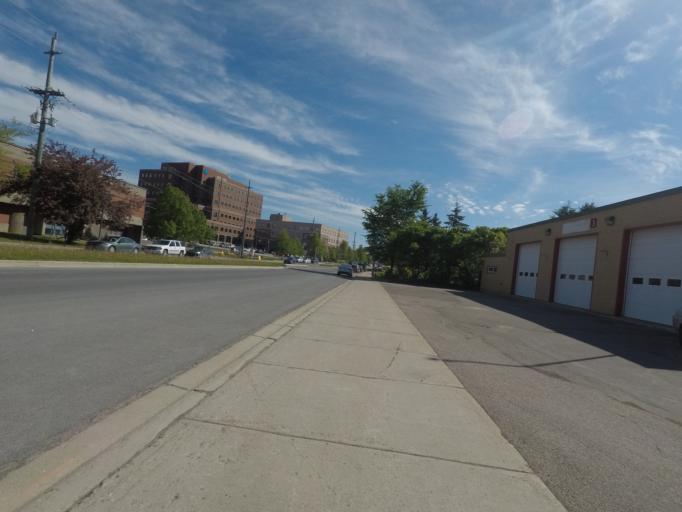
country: CA
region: New Brunswick
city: Moncton
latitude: 46.0868
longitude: -64.7750
